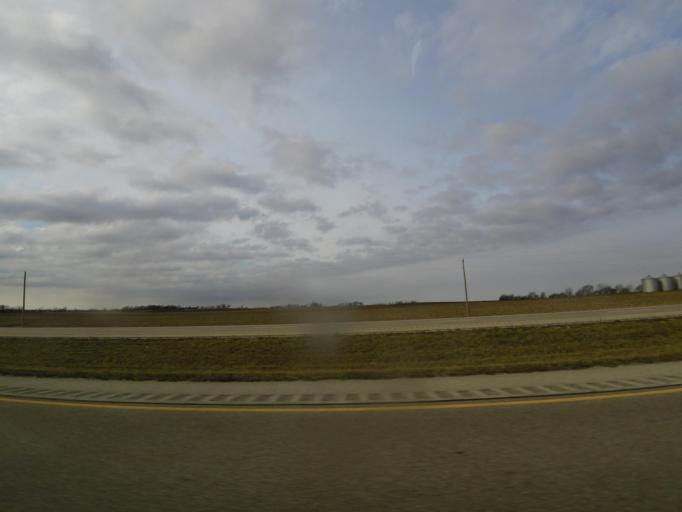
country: US
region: Illinois
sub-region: Christian County
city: Assumption
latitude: 39.4685
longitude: -89.0439
